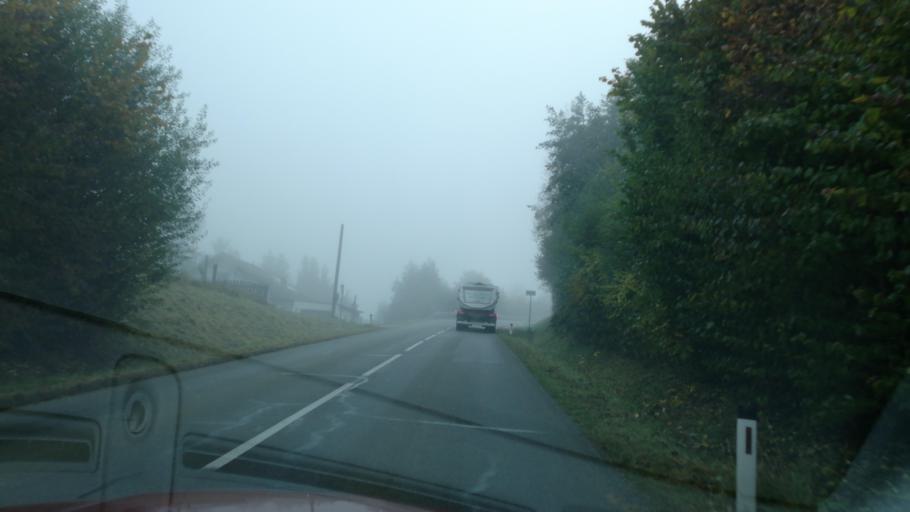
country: AT
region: Upper Austria
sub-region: Politischer Bezirk Grieskirchen
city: Bad Schallerbach
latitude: 48.1812
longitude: 13.9059
